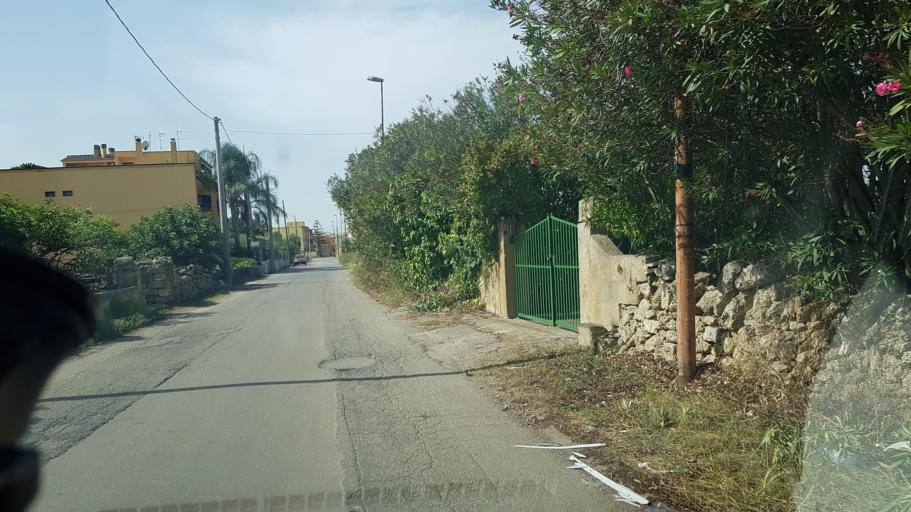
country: IT
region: Apulia
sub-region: Provincia di Brindisi
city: Mesagne
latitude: 40.5645
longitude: 17.8199
